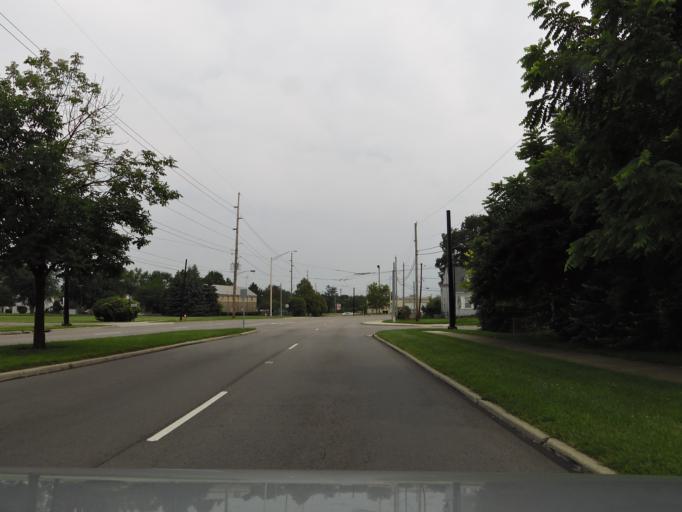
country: US
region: Ohio
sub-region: Montgomery County
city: Oakwood
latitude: 39.7204
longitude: -84.1242
